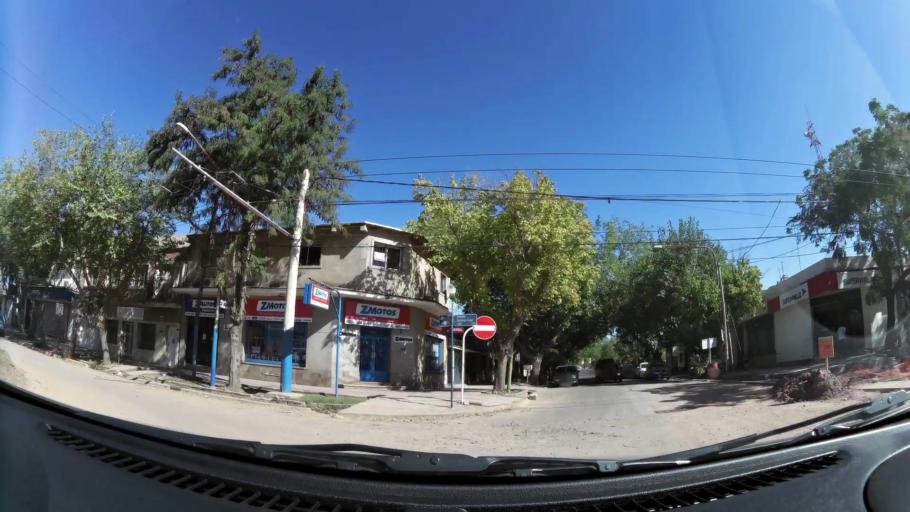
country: AR
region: Mendoza
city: Mendoza
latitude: -32.8895
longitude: -68.8129
